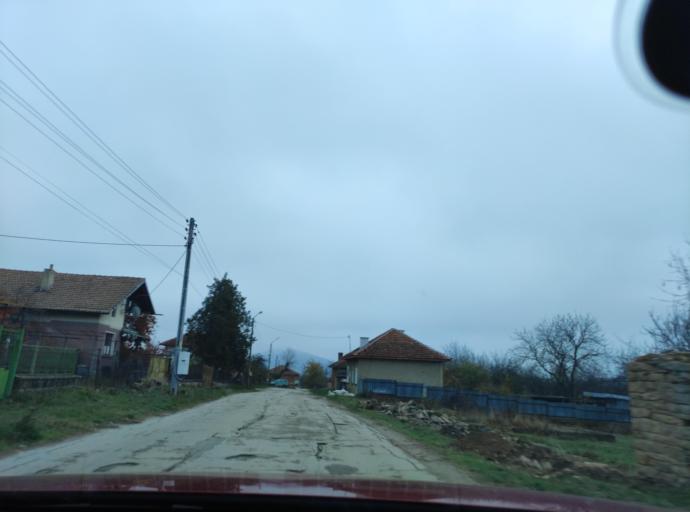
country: BG
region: Lovech
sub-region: Obshtina Yablanitsa
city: Yablanitsa
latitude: 43.0926
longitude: 24.0794
